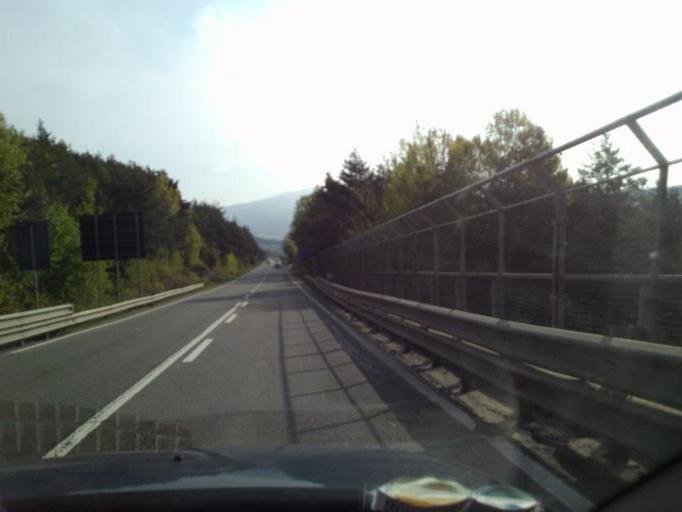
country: IT
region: Trentino-Alto Adige
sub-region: Bolzano
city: Naz-Sciaves - Natz-Schabs
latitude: 46.7668
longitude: 11.6472
